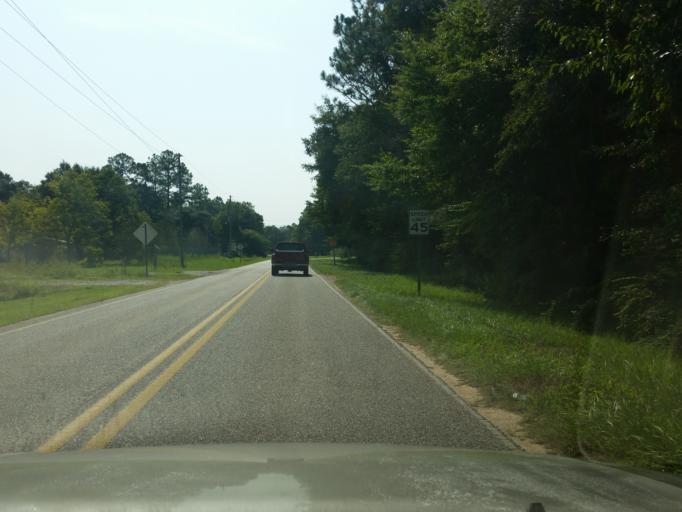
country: US
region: Alabama
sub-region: Baldwin County
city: Elberta
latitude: 30.5143
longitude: -87.4733
